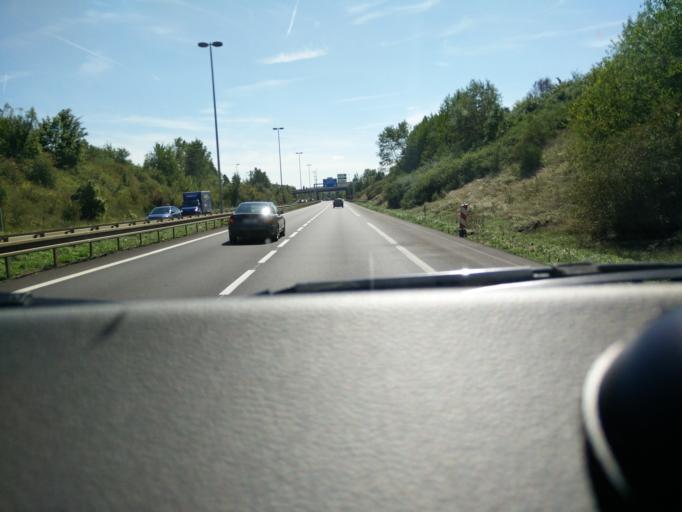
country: FR
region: Lorraine
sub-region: Departement de la Moselle
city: Terville
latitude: 49.3671
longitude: 6.1067
